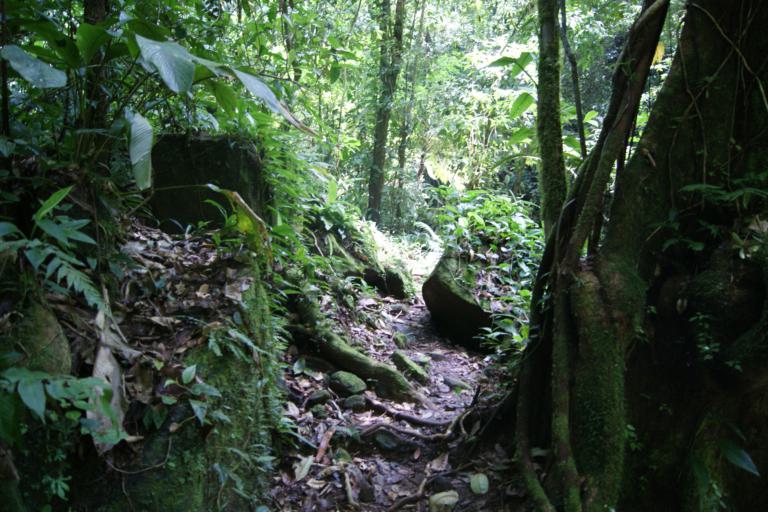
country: BR
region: Sao Paulo
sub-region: Mongagua
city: Mongagua
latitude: -24.0285
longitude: -46.7063
